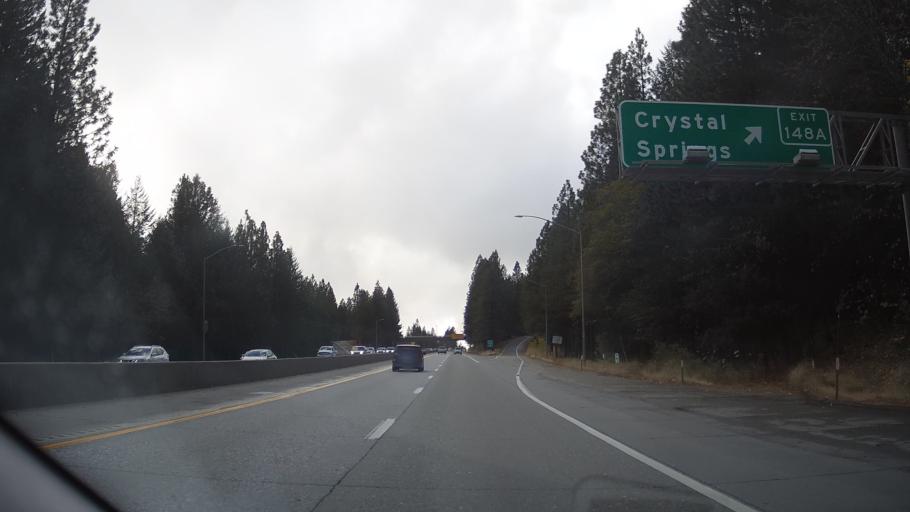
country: US
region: California
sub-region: Placer County
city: Foresthill
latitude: 39.2113
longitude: -120.7828
